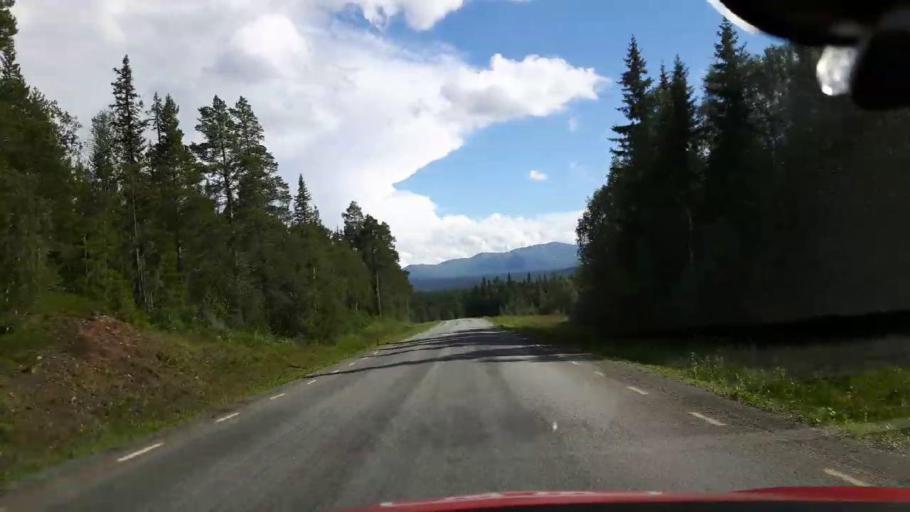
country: SE
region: Jaemtland
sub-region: Are Kommun
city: Are
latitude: 63.2262
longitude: 13.1603
